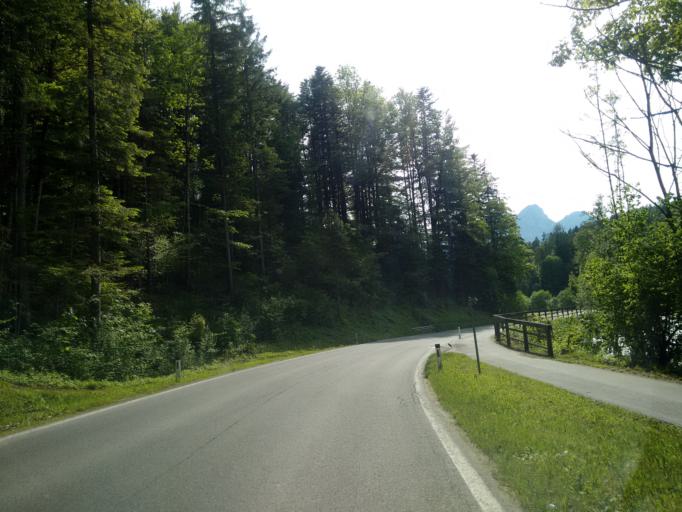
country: AT
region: Styria
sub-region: Politischer Bezirk Liezen
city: Bad Aussee
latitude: 47.6168
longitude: 13.7992
